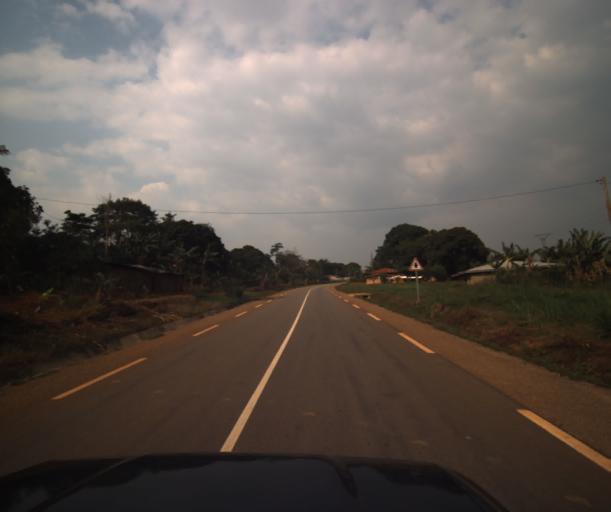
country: CM
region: Centre
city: Mbankomo
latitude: 3.7041
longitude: 11.3747
